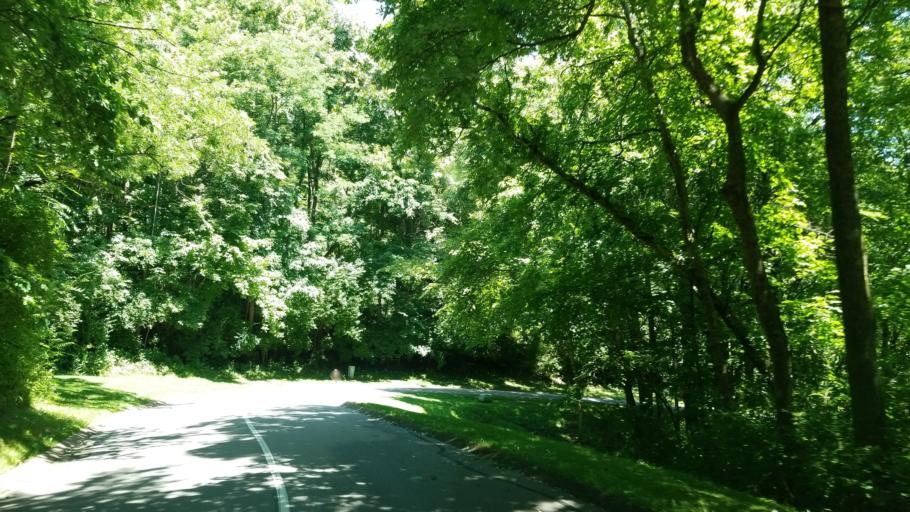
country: US
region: Tennessee
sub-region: Davidson County
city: Forest Hills
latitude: 36.0531
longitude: -86.8220
